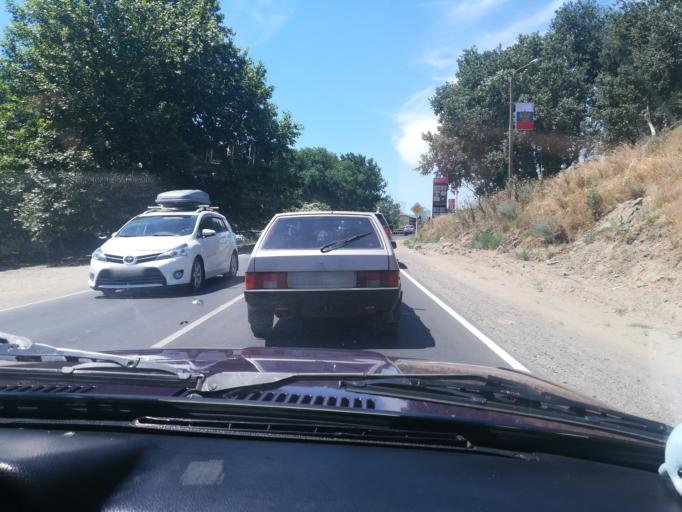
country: RU
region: Krasnodarskiy
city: Vityazevo
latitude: 44.9760
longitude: 37.2744
